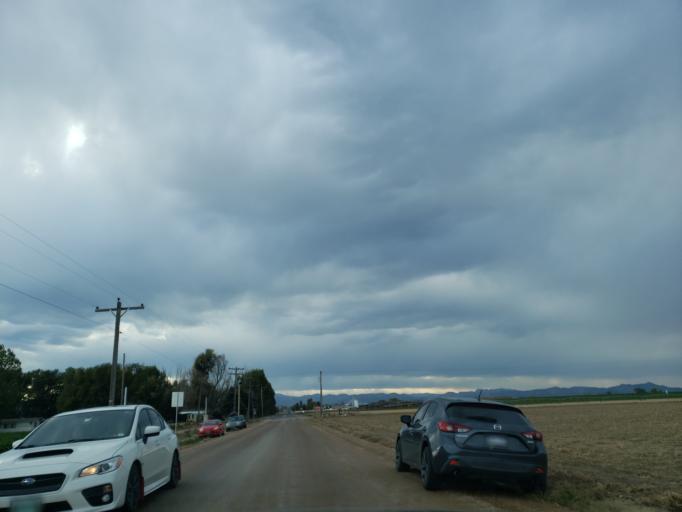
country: US
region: Colorado
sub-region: Larimer County
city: Wellington
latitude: 40.6391
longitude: -105.0182
